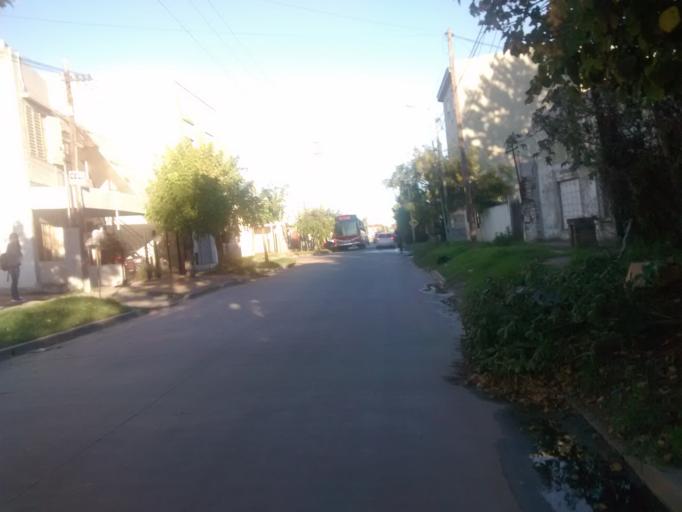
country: AR
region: Buenos Aires
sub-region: Partido de La Plata
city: La Plata
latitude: -34.9026
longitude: -57.9204
